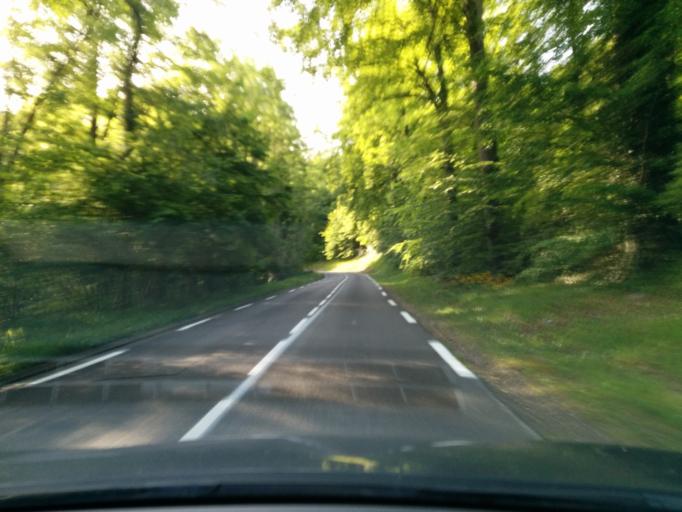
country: FR
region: Haute-Normandie
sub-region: Departement de la Seine-Maritime
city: La Feuillie
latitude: 49.4073
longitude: 1.4823
